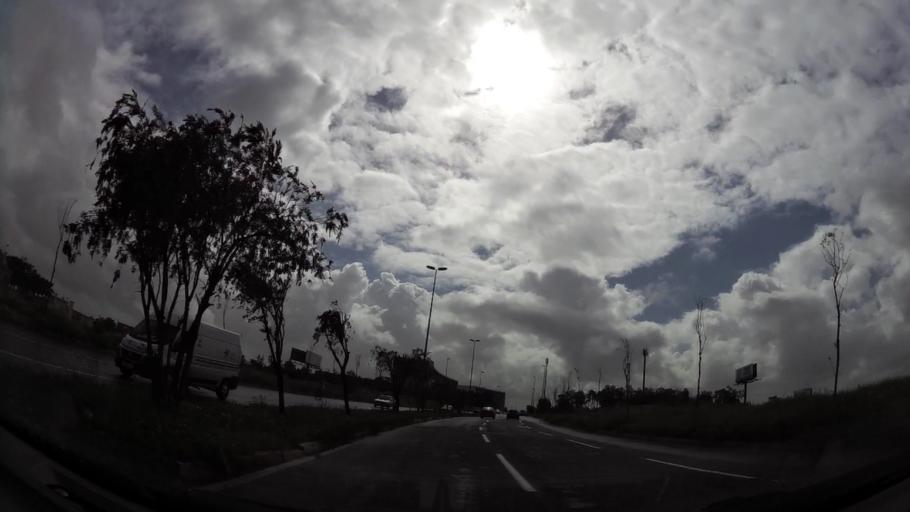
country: MA
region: Grand Casablanca
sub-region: Casablanca
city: Casablanca
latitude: 33.5311
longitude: -7.6359
